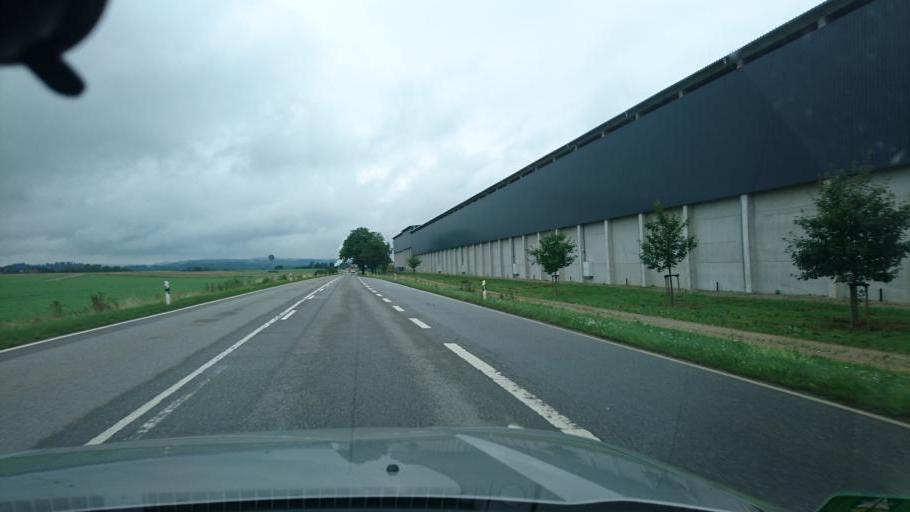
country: DE
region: Baden-Wuerttemberg
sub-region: Freiburg Region
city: Deisslingen
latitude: 48.1139
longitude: 8.6156
